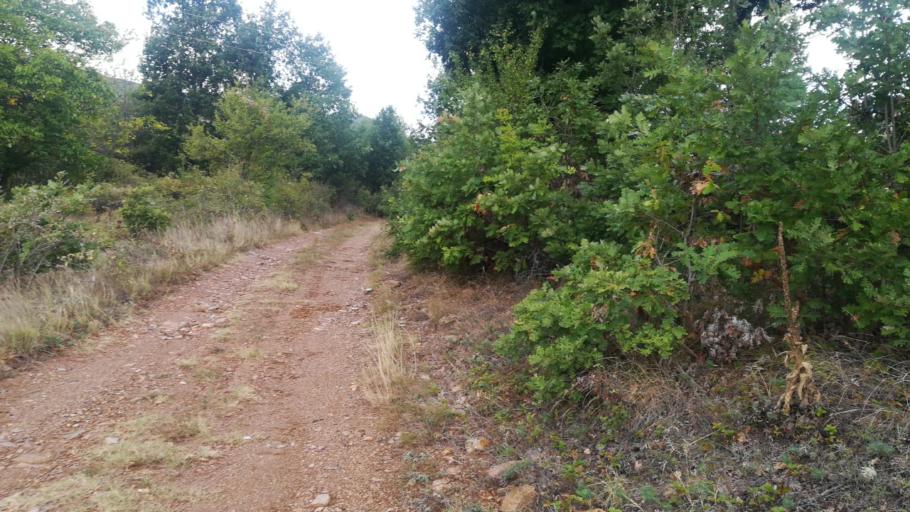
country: MK
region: Makedonska Kamenica
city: Makedonska Kamenica
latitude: 42.0165
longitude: 22.5750
